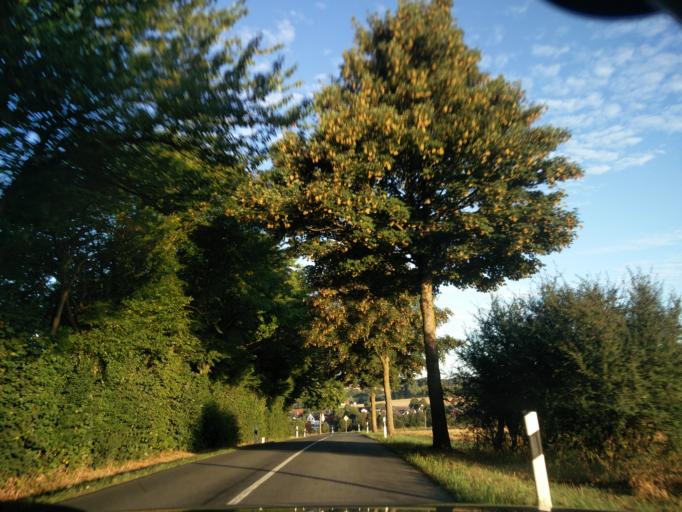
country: DE
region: North Rhine-Westphalia
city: Lichtenau
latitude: 51.6721
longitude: 8.9327
